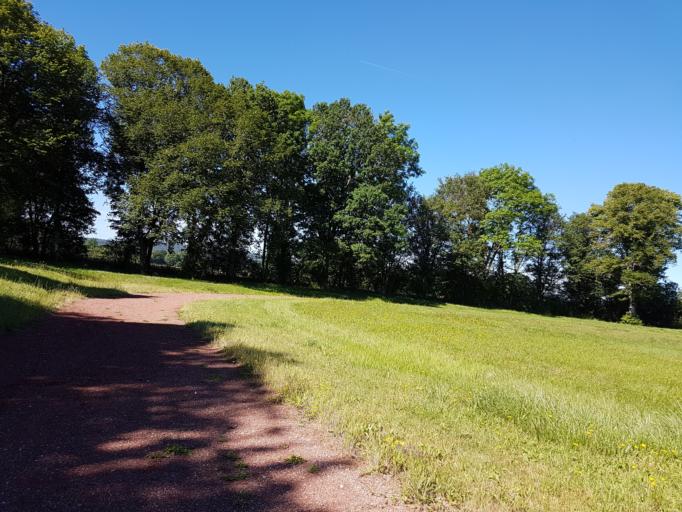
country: FR
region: Bourgogne
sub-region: Departement de Saone-et-Loire
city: Epinac
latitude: 46.9850
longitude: 4.5044
